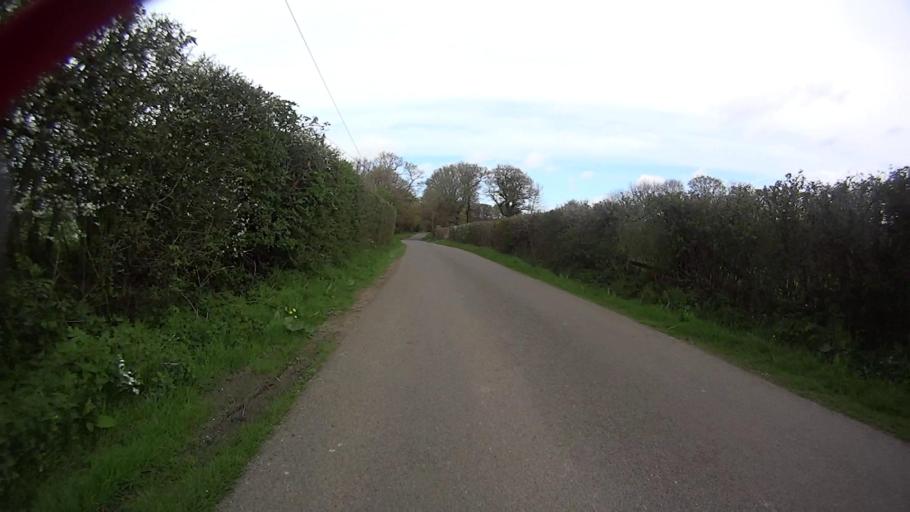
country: GB
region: England
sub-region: West Sussex
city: Bewbush
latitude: 51.1309
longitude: -0.2573
